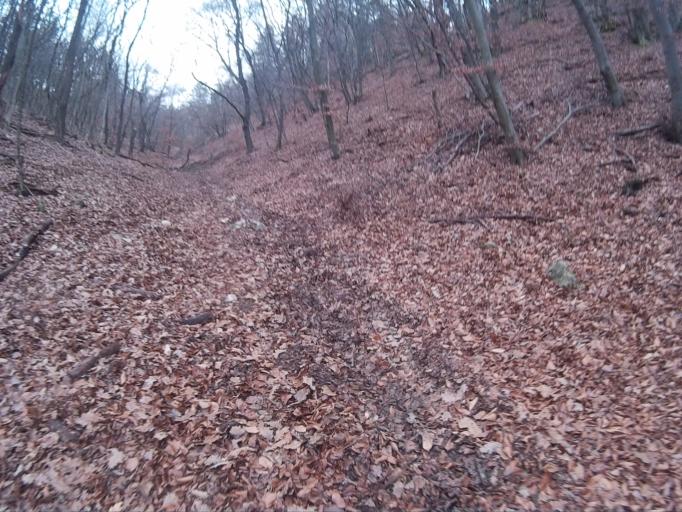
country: HU
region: Veszprem
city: Tapolca
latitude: 46.9709
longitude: 17.4855
